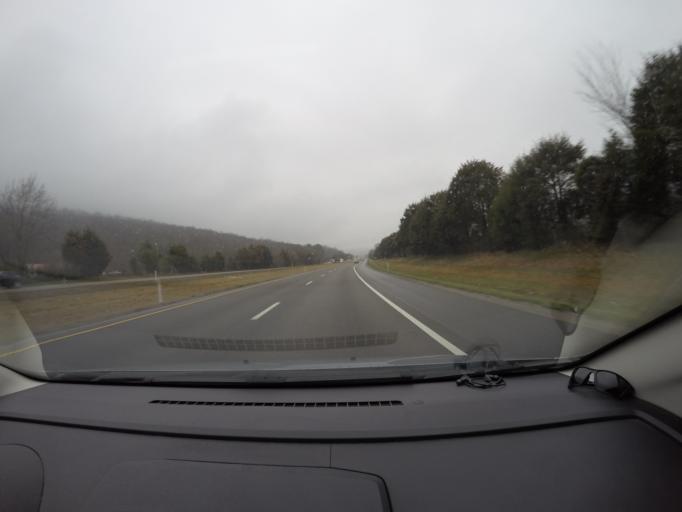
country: US
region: Tennessee
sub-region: Marion County
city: Kimball
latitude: 35.0985
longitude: -85.7373
